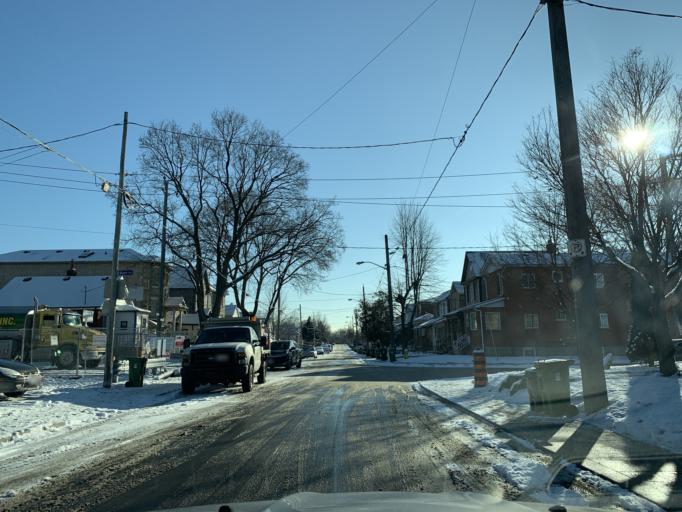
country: CA
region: Ontario
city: Toronto
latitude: 43.6864
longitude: -79.4866
